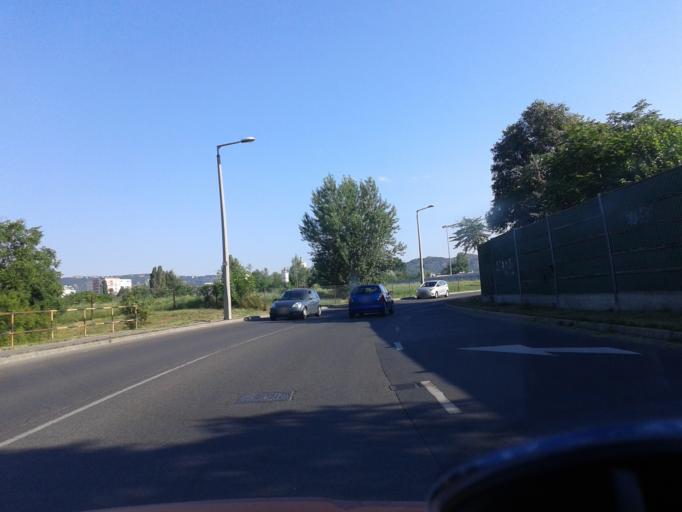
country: HU
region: Budapest
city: Budapest XI. keruelet
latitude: 47.4570
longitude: 19.0231
